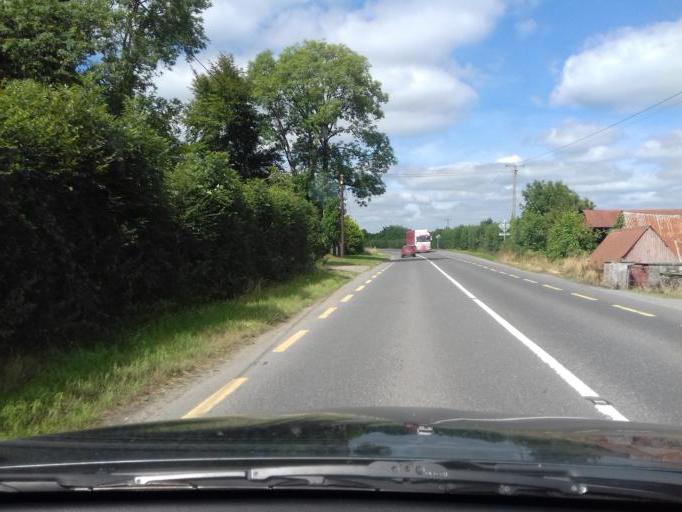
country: IE
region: Leinster
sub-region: Wicklow
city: Baltinglass
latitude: 53.0069
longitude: -6.6428
